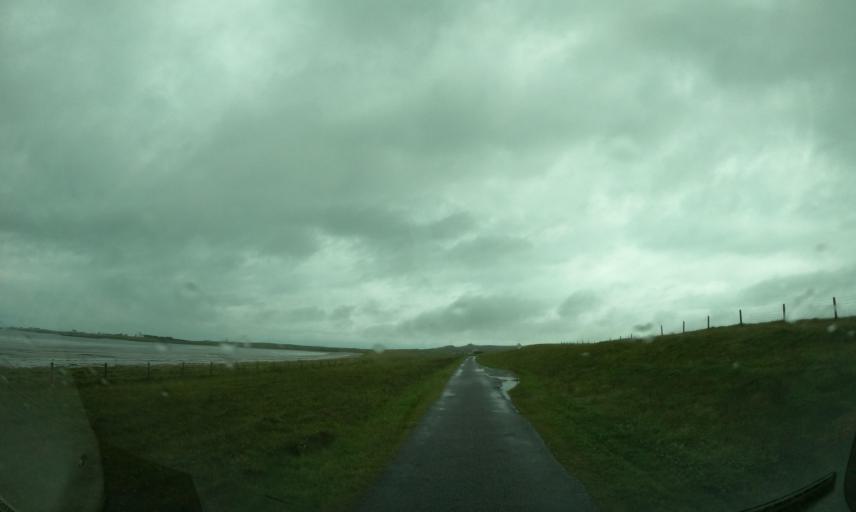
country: GB
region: Scotland
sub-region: Eilean Siar
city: Barra
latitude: 56.5174
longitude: -6.8133
